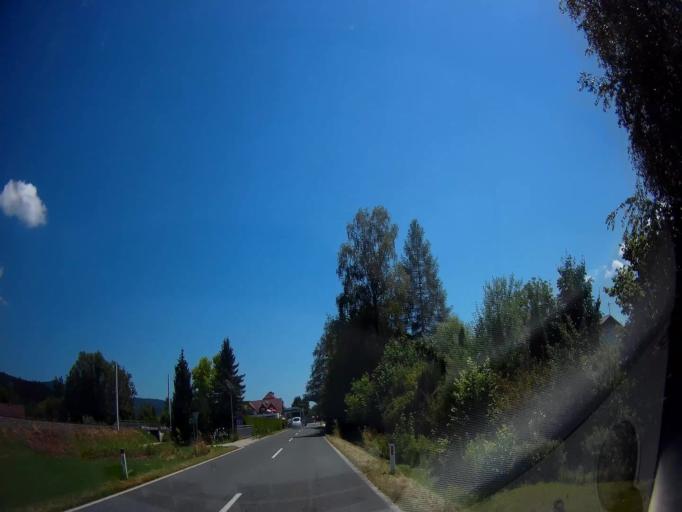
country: AT
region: Carinthia
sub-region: Politischer Bezirk Volkermarkt
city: Feistritz ob Bleiburg
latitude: 46.5762
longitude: 14.7740
